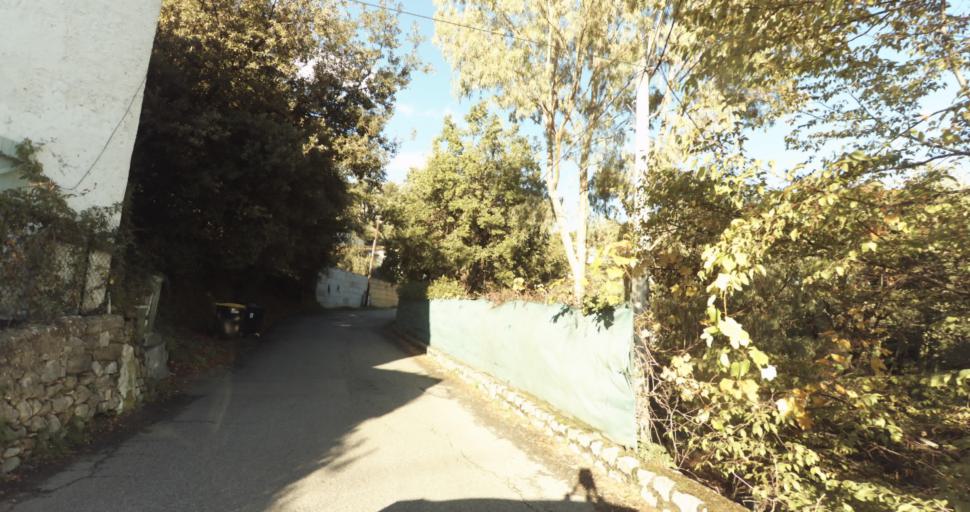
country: FR
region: Provence-Alpes-Cote d'Azur
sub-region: Departement des Alpes-Maritimes
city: Saint-Jeannet
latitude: 43.7355
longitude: 7.1310
